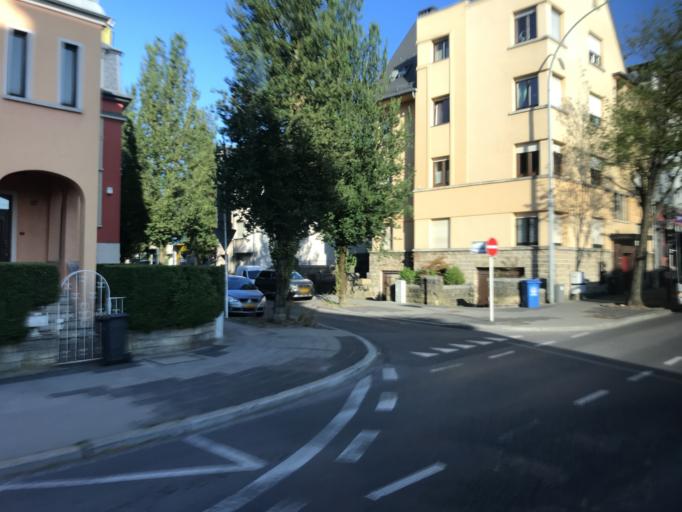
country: LU
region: Luxembourg
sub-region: Canton de Luxembourg
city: Luxembourg
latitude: 49.5938
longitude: 6.1385
